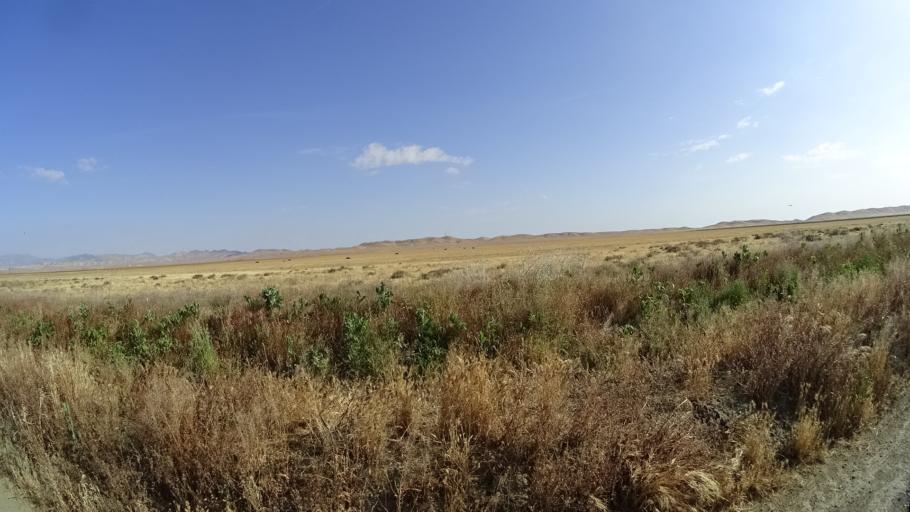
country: US
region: California
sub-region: Kings County
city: Avenal
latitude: 35.8179
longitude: -120.0730
